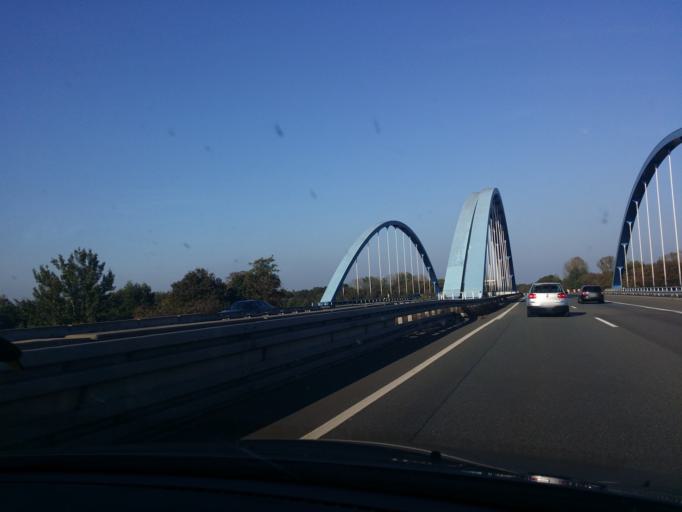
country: DE
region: North Rhine-Westphalia
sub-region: Regierungsbezirk Munster
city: Ladbergen
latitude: 52.1203
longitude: 7.7085
